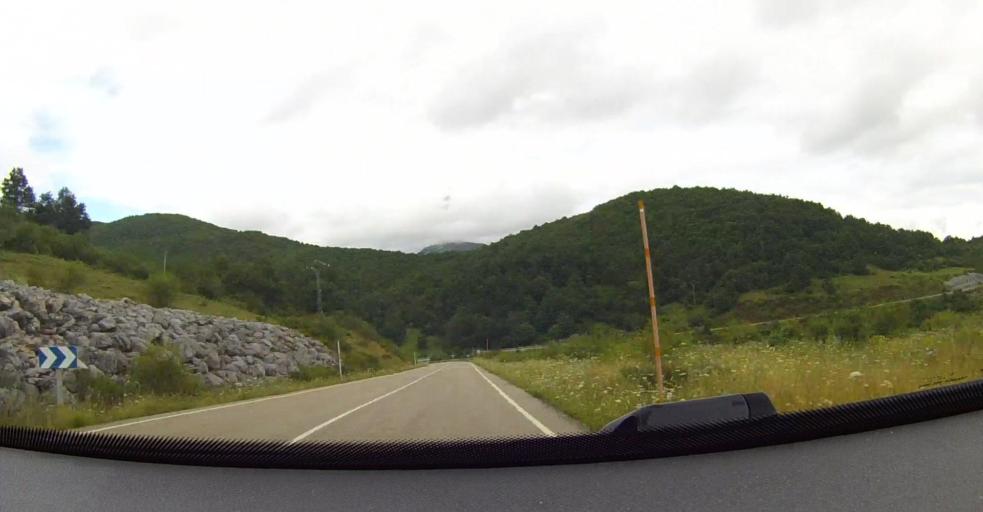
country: ES
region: Castille and Leon
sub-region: Provincia de Leon
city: Buron
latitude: 43.0223
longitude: -5.0394
